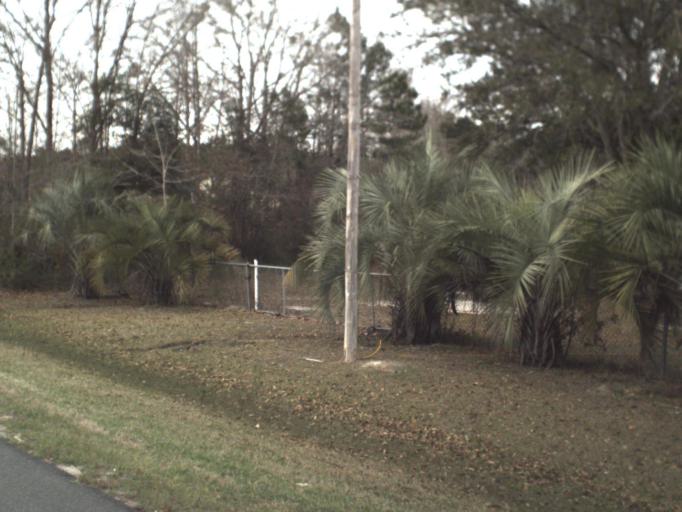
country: US
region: Florida
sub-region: Gulf County
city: Wewahitchka
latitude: 30.1180
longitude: -85.2093
